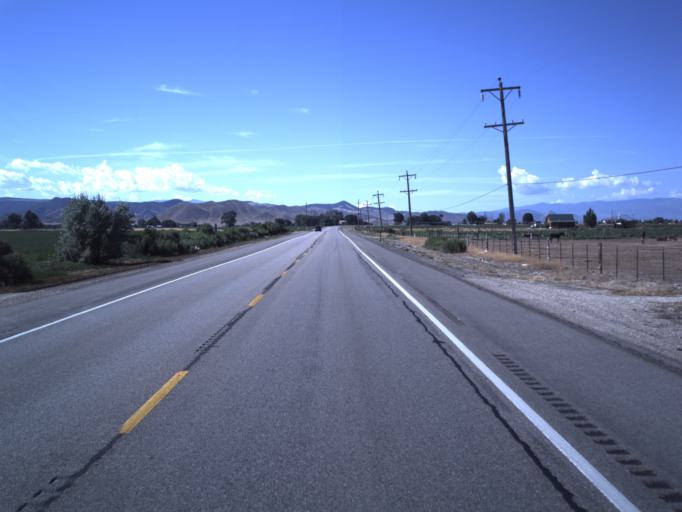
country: US
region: Utah
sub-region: Sanpete County
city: Centerfield
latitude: 39.0673
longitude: -111.8209
